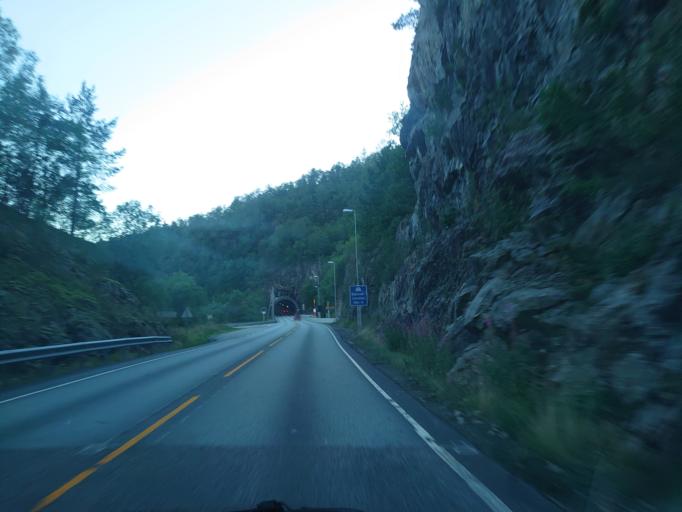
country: NO
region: Hordaland
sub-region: Osteroy
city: Lonevag
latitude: 60.6383
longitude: 5.4908
